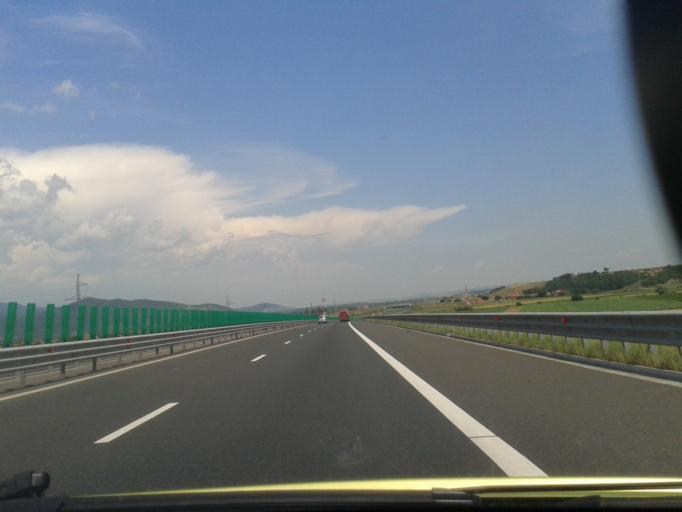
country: RO
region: Alba
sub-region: Comuna Sibot
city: Sibot
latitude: 45.9175
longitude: 23.3294
